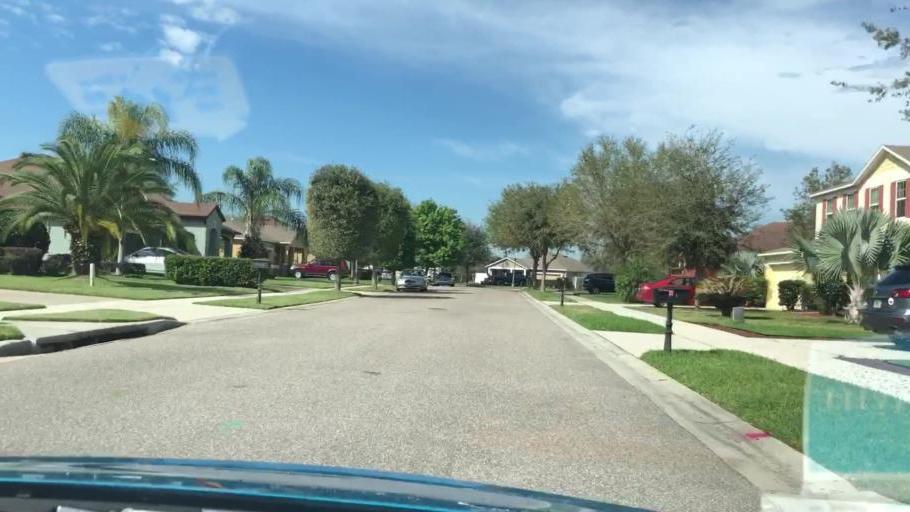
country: US
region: Florida
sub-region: Volusia County
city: Deltona
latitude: 28.8734
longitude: -81.2497
